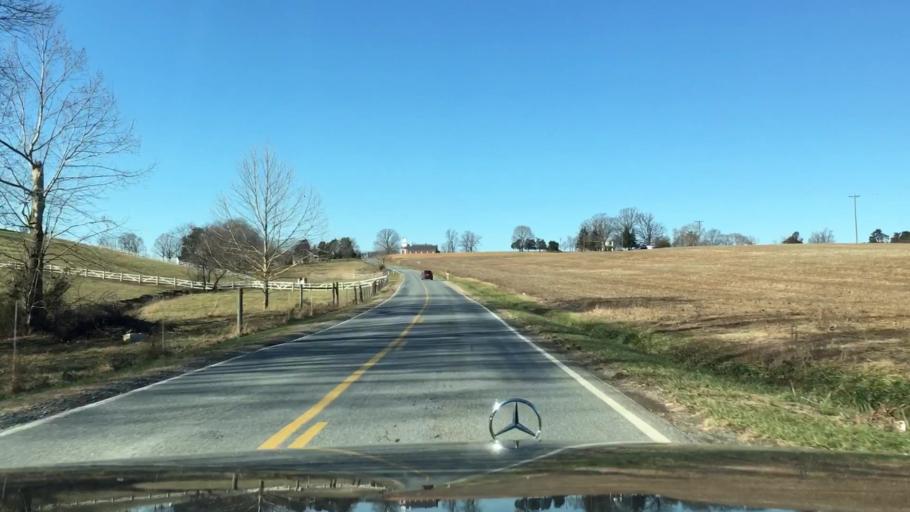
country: US
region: Virginia
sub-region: Pittsylvania County
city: Motley
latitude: 37.1889
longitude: -79.4215
